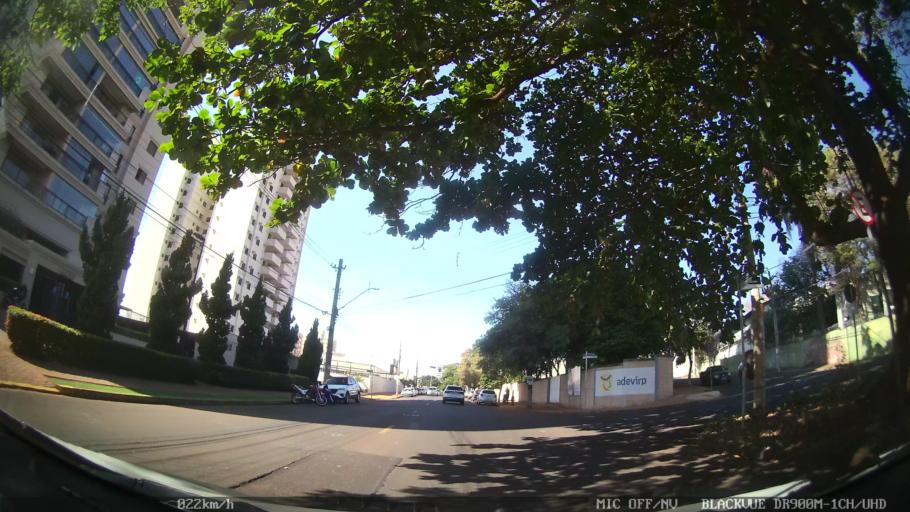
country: BR
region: Sao Paulo
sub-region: Ribeirao Preto
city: Ribeirao Preto
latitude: -21.2036
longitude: -47.7996
